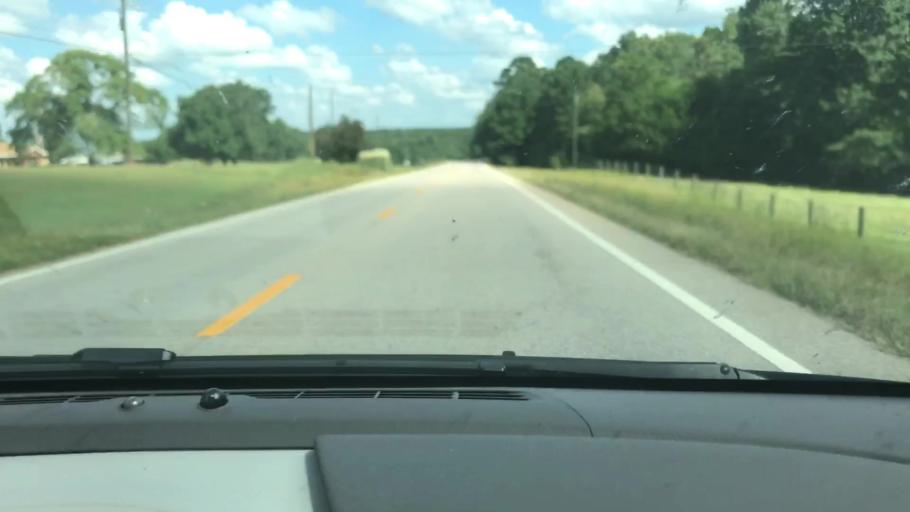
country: US
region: Georgia
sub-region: Troup County
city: La Grange
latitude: 32.8895
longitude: -85.0334
